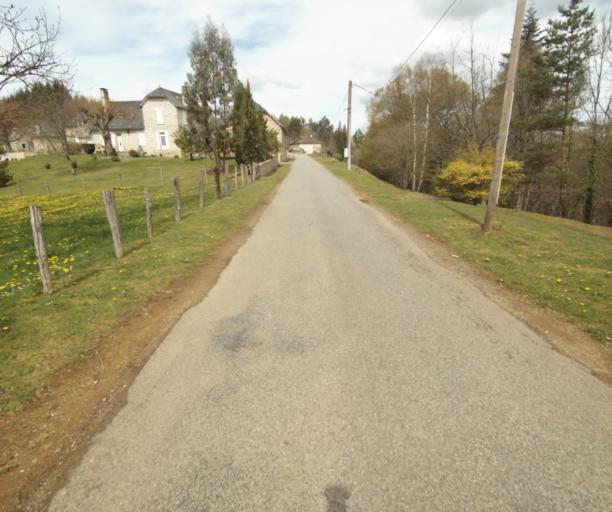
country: FR
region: Limousin
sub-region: Departement de la Correze
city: Laguenne
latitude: 45.2111
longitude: 1.8623
